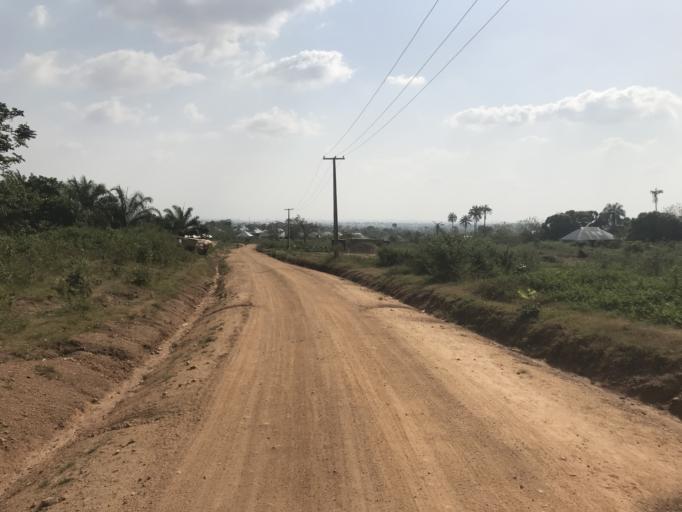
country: NG
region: Osun
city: Osogbo
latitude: 7.8470
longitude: 4.5815
